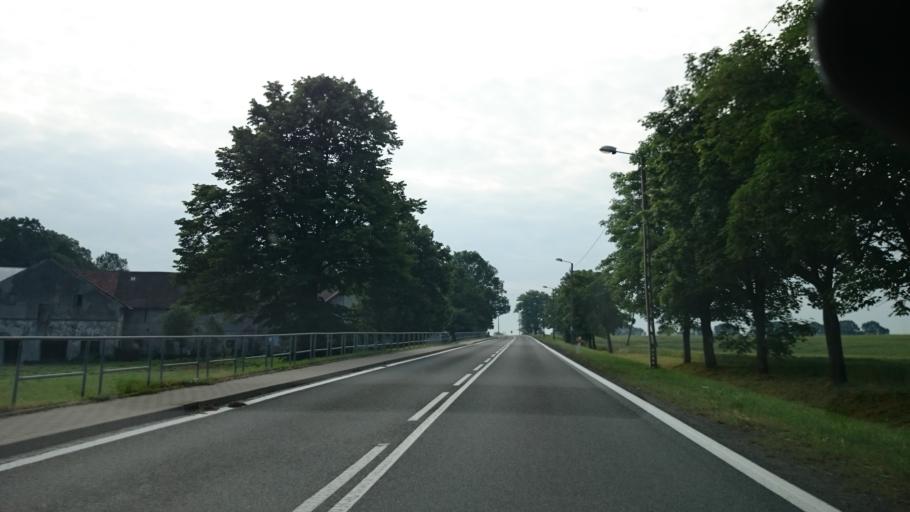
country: PL
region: Silesian Voivodeship
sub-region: Powiat gliwicki
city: Toszek
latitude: 50.4705
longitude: 18.4710
